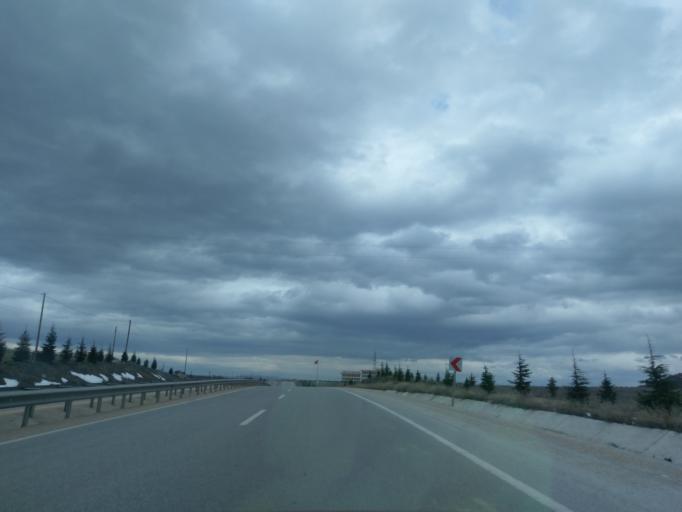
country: TR
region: Eskisehir
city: Eskisehir
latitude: 39.7372
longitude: 30.3888
